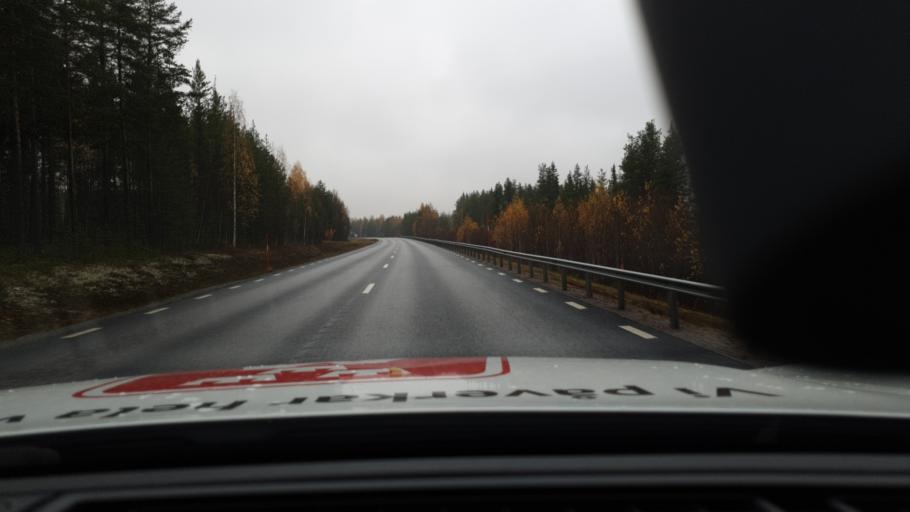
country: SE
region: Norrbotten
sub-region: Overkalix Kommun
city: OEverkalix
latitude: 66.6388
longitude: 22.2003
